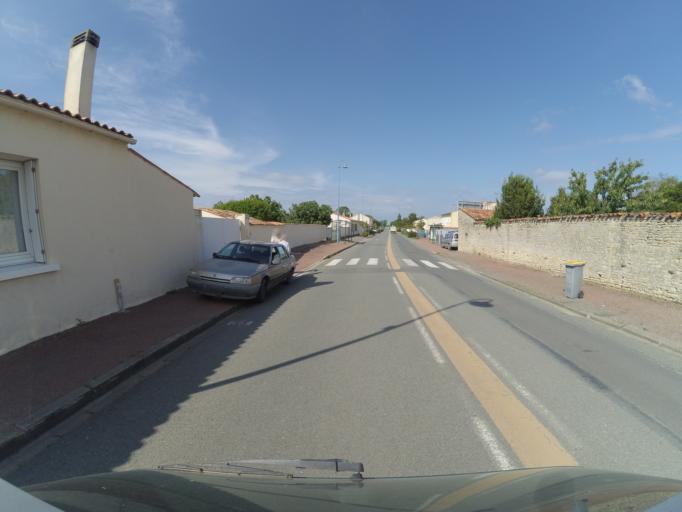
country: FR
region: Poitou-Charentes
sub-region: Departement de la Charente-Maritime
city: Andilly
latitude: 46.2434
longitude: -1.0652
